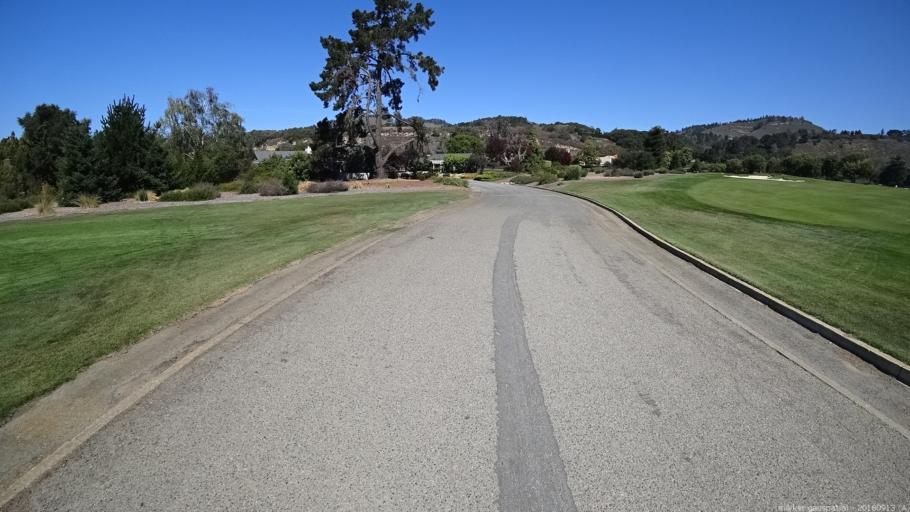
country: US
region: California
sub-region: Monterey County
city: Del Rey Oaks
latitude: 36.5311
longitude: -121.8546
